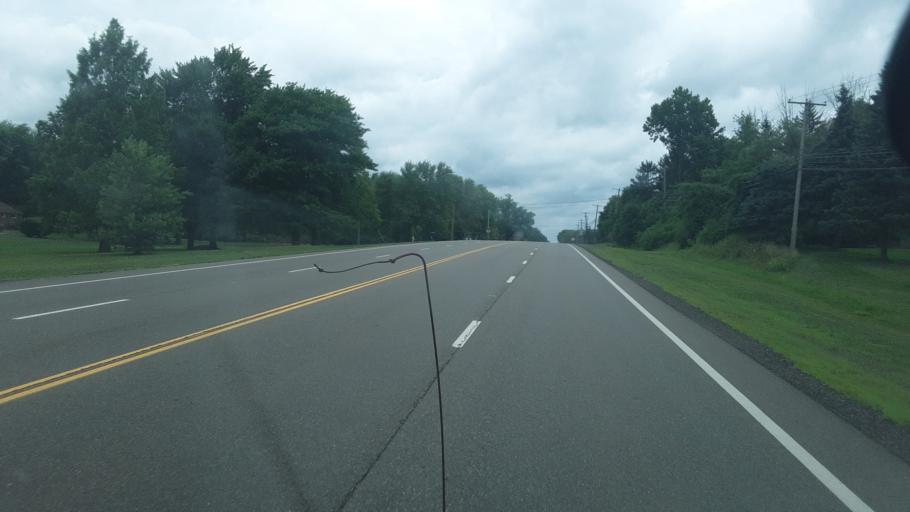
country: US
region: Ohio
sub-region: Trumbull County
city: Churchill
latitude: 41.2254
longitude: -80.6638
